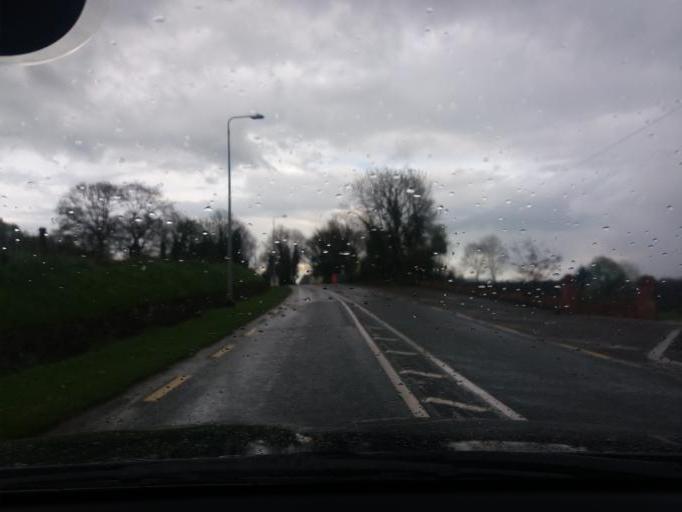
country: IE
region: Ulster
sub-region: An Cabhan
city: Ballyconnell
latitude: 54.1198
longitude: -7.6718
